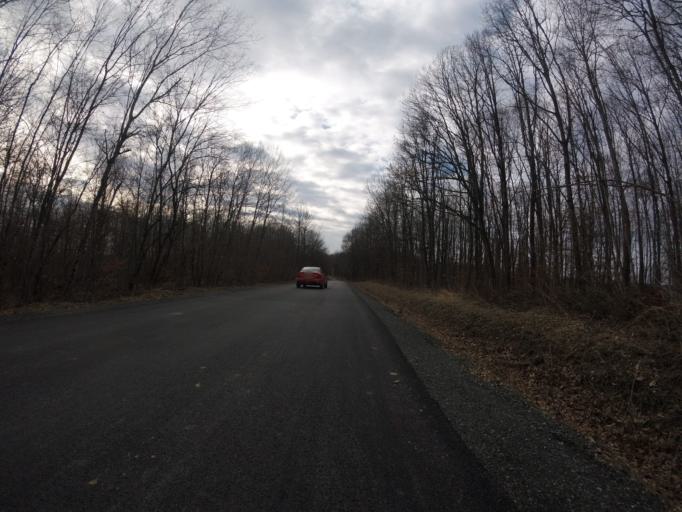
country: HR
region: Sisacko-Moslavacka
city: Glina
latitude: 45.4923
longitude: 16.0455
